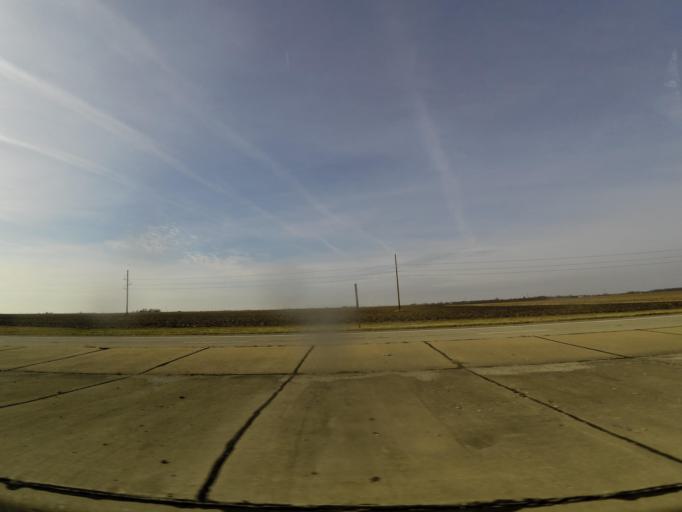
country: US
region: Illinois
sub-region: De Witt County
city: Clinton
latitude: 40.2237
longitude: -88.9648
